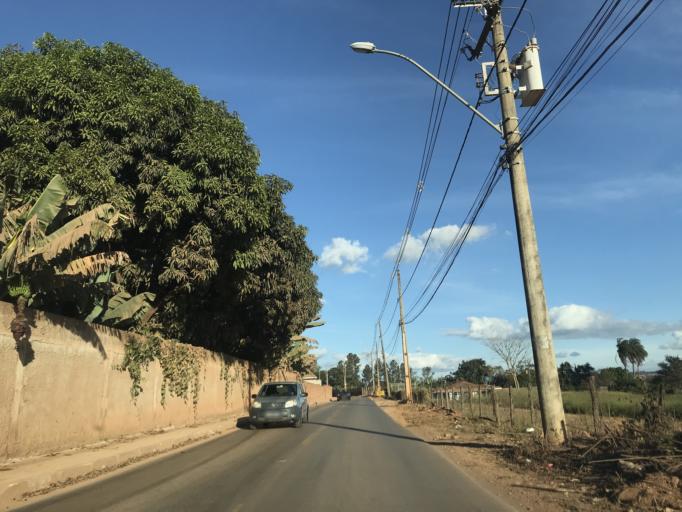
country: BR
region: Federal District
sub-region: Brasilia
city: Brasilia
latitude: -15.8819
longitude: -47.7754
